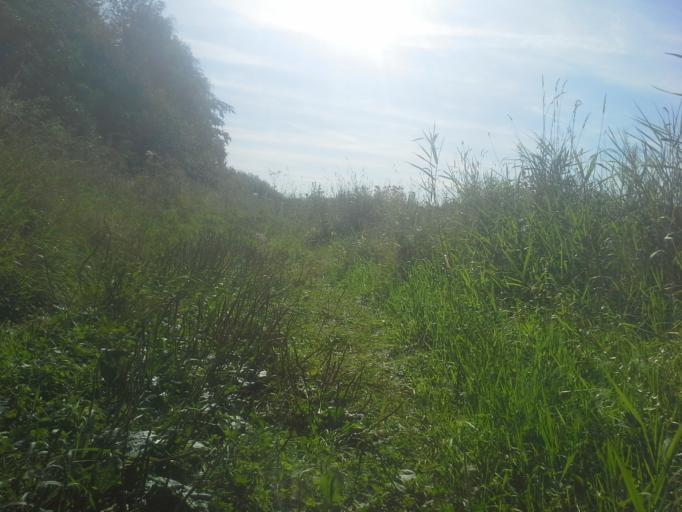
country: RU
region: Moskovskaya
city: Aprelevka
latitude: 55.4506
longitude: 37.0796
